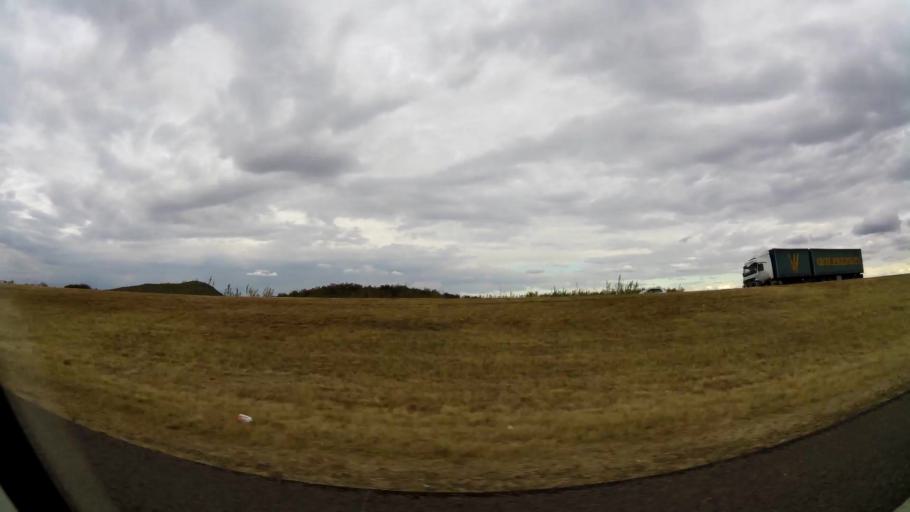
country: ZA
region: Limpopo
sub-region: Waterberg District Municipality
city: Modimolle
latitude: -24.6798
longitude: 28.5579
